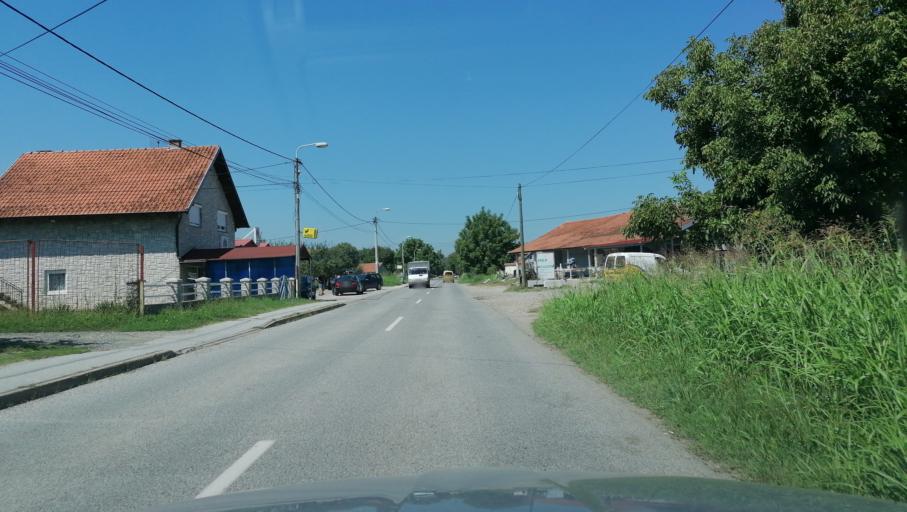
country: RS
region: Central Serbia
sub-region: Raski Okrug
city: Kraljevo
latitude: 43.6903
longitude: 20.6016
